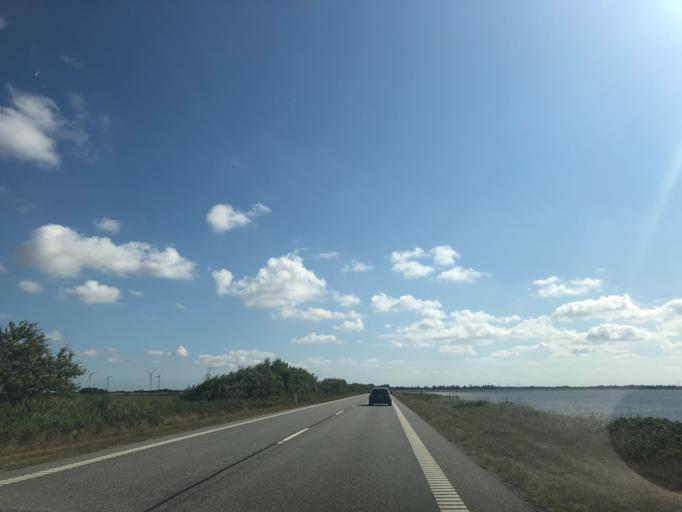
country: DK
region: North Denmark
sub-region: Jammerbugt Kommune
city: Fjerritslev
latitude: 57.0368
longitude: 9.1175
